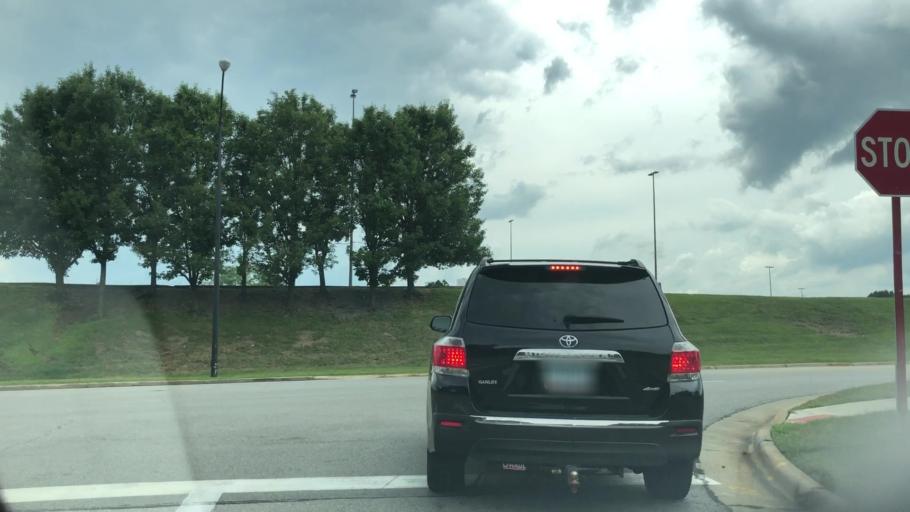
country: US
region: Ohio
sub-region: Summit County
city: Fairlawn
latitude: 41.1343
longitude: -81.6143
